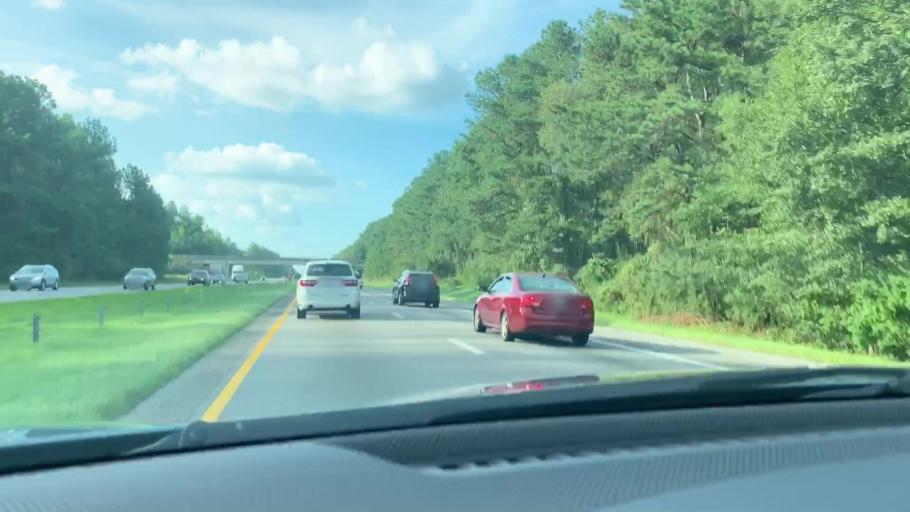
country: US
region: South Carolina
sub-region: Orangeburg County
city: Brookdale
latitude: 33.5325
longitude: -80.8024
